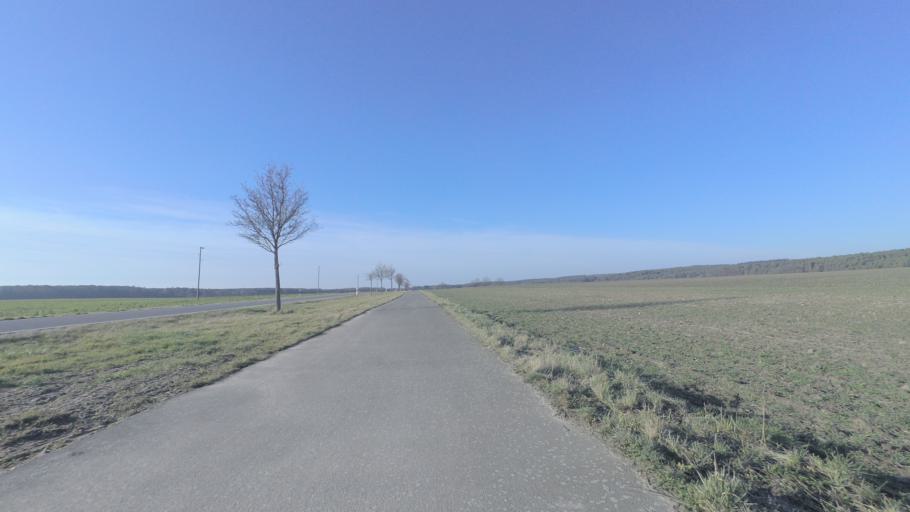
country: DE
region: Brandenburg
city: Ihlow
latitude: 51.9929
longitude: 13.3543
